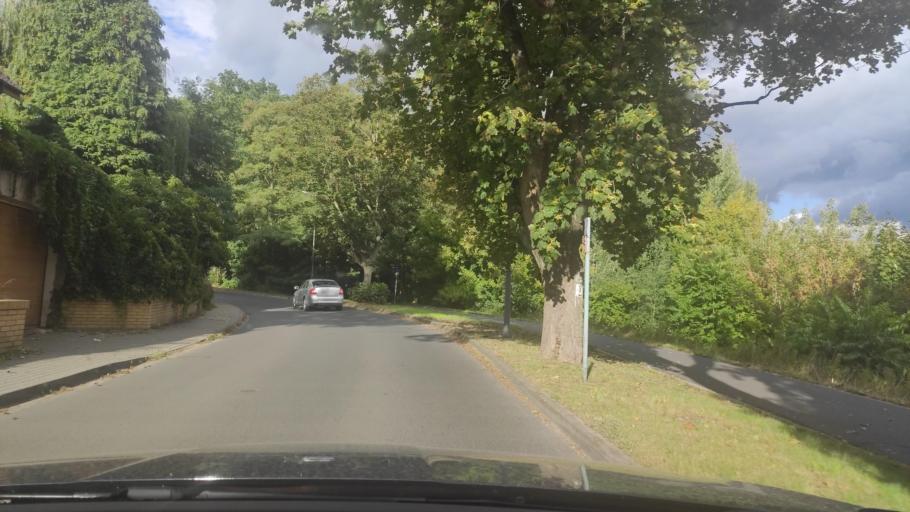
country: PL
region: Greater Poland Voivodeship
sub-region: Powiat poznanski
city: Swarzedz
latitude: 52.4100
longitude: 17.0484
